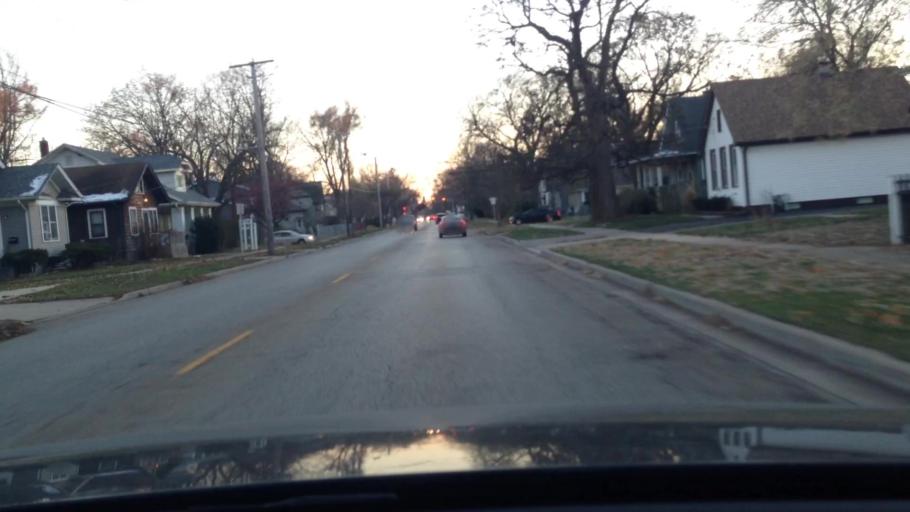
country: US
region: Illinois
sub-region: Kane County
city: Elgin
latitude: 42.0493
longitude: -88.2677
